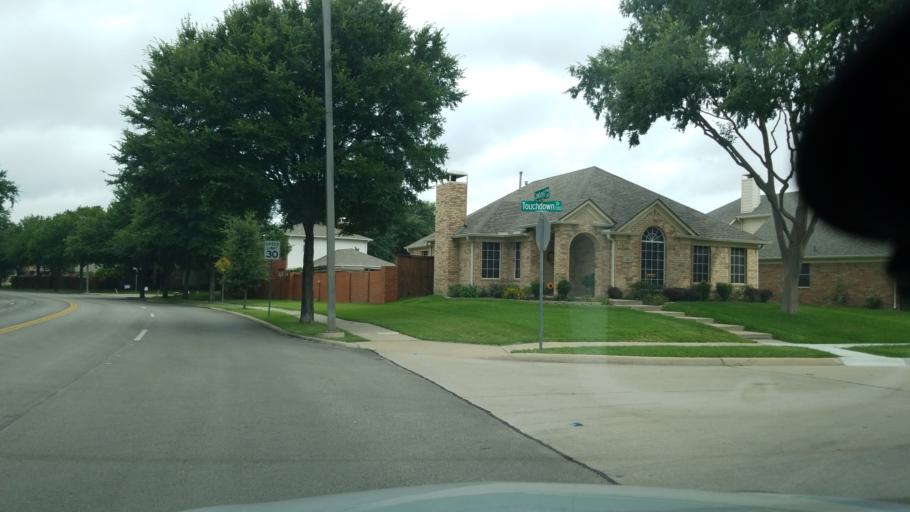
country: US
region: Texas
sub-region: Dallas County
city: Farmers Branch
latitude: 32.9461
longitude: -96.9465
